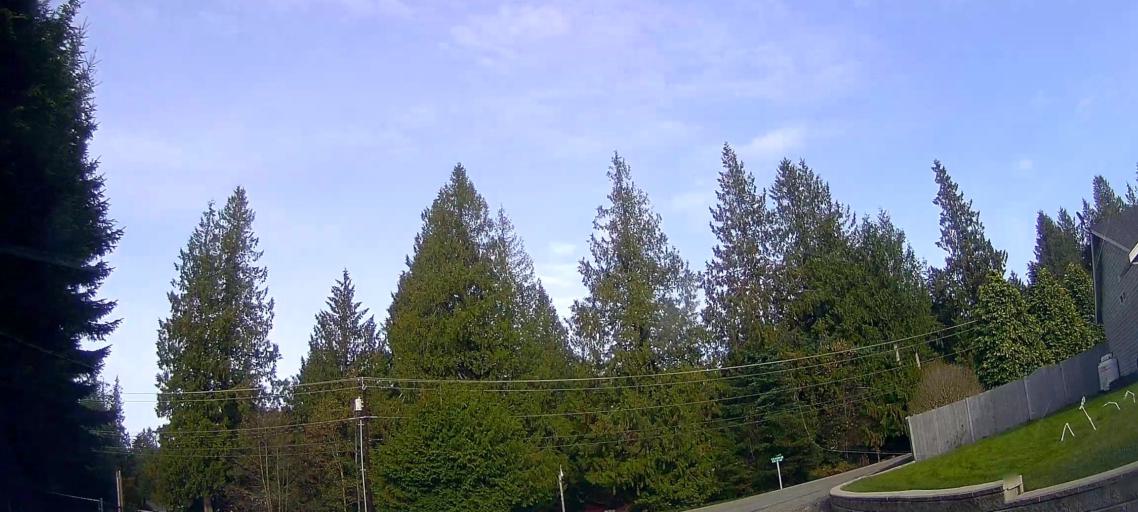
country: US
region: Washington
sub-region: Snohomish County
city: Stanwood
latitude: 48.2804
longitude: -122.3394
